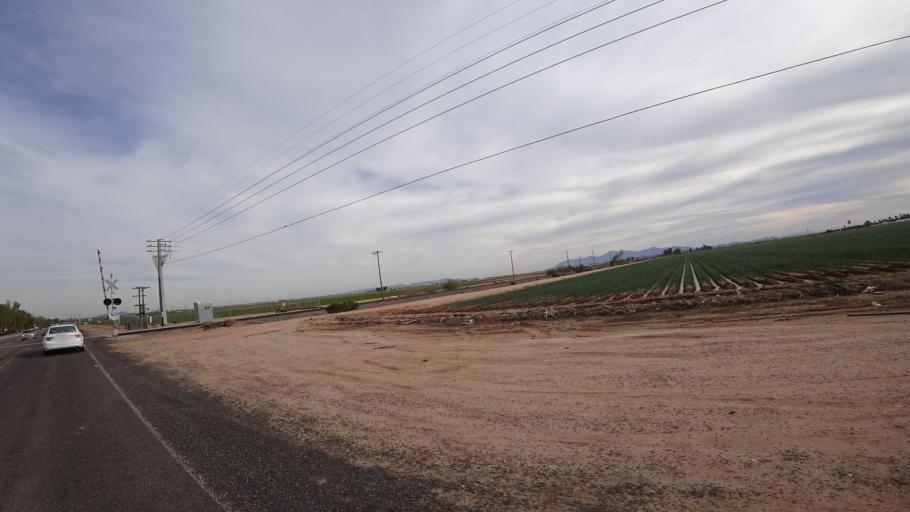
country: US
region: Arizona
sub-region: Maricopa County
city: El Mirage
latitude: 33.5802
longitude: -112.3512
